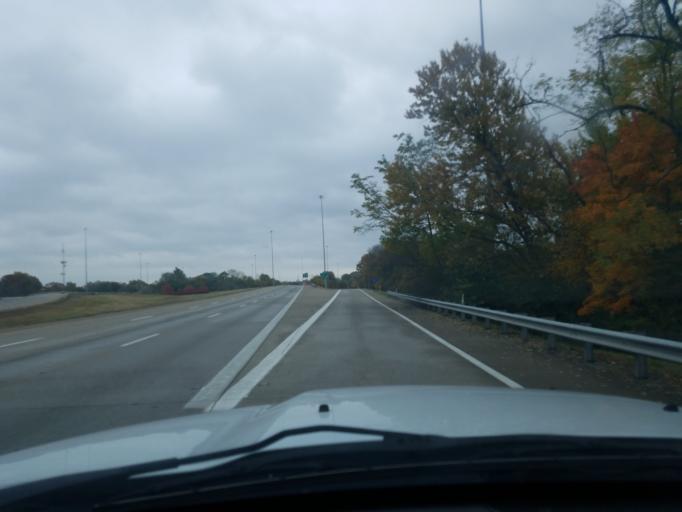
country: US
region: Kentucky
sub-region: Jefferson County
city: Shively
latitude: 38.1855
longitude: -85.8198
